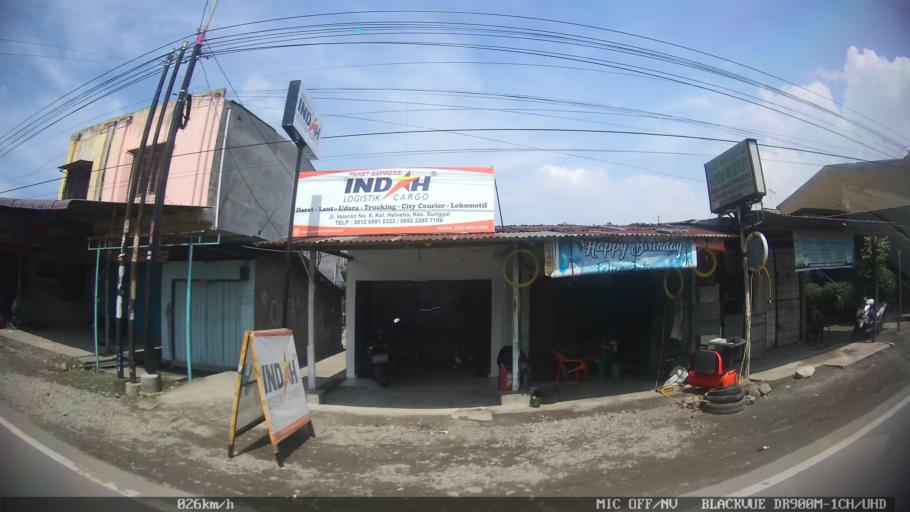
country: ID
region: North Sumatra
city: Medan
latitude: 3.6406
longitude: 98.6579
